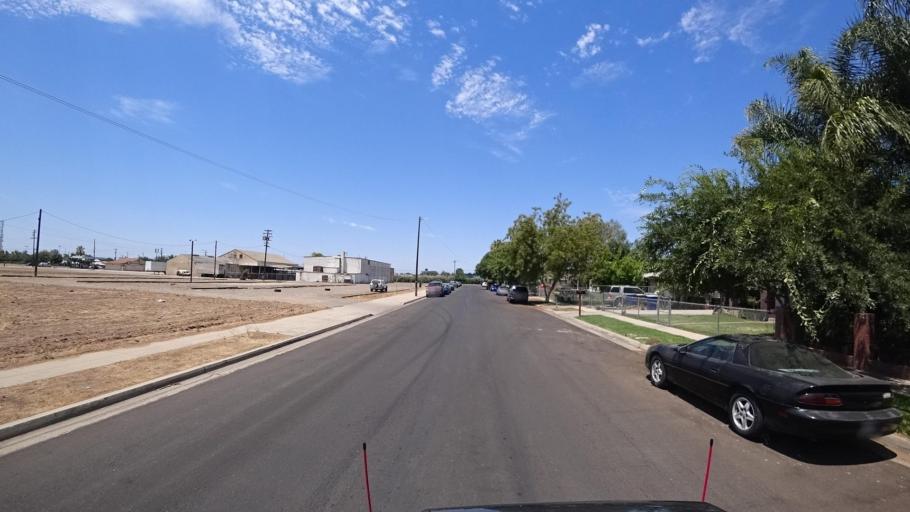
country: US
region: California
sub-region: Fresno County
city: Fresno
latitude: 36.7304
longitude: -119.7437
